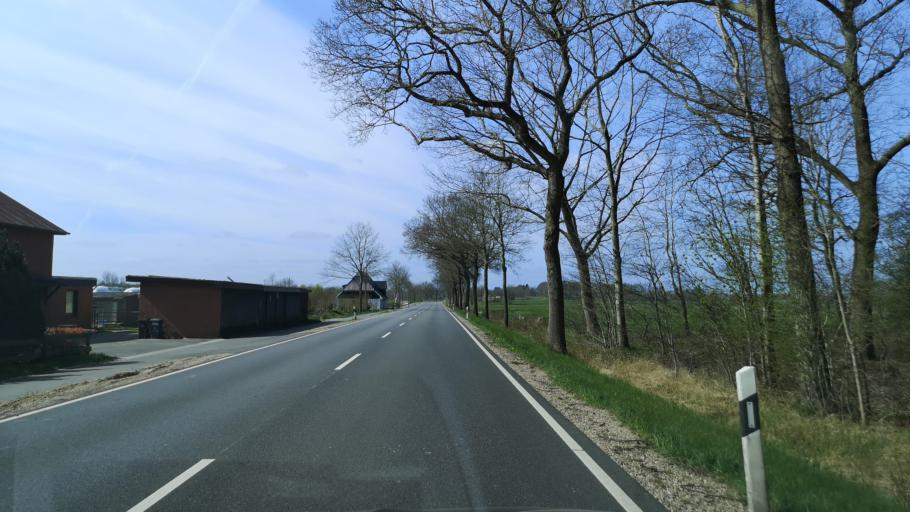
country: DE
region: Schleswig-Holstein
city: Prinzenmoor
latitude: 54.2222
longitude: 9.4707
